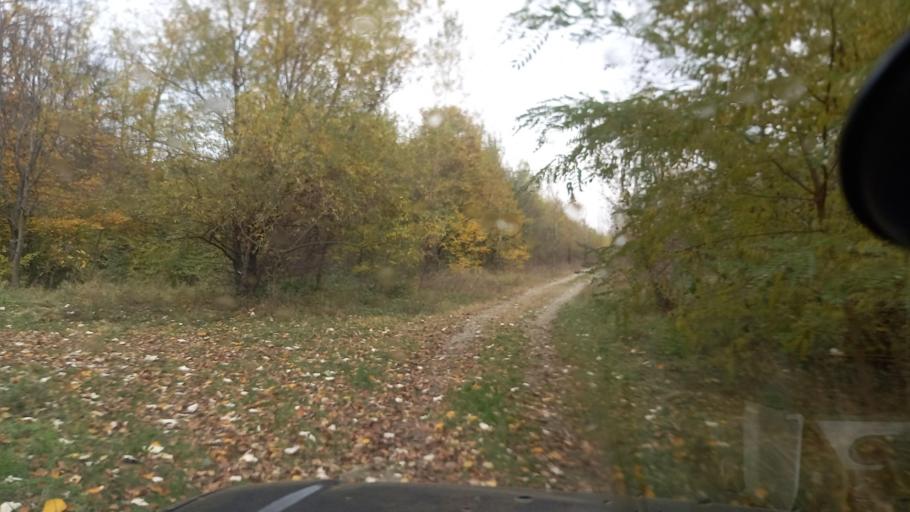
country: RU
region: Krasnodarskiy
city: Shedok
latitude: 44.1704
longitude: 40.8470
